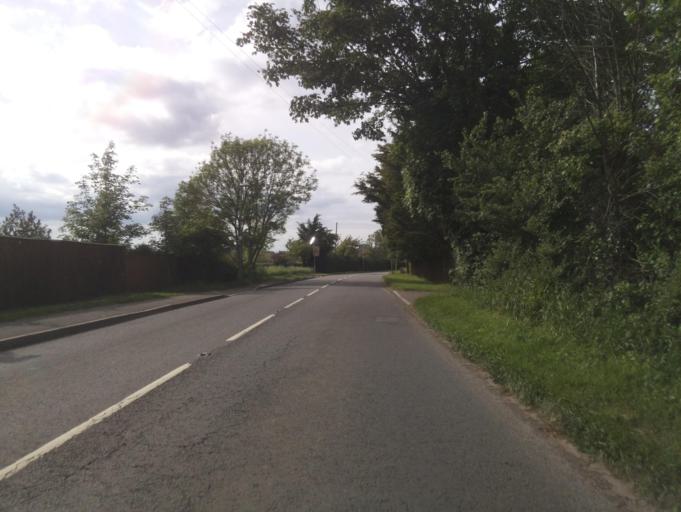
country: GB
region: England
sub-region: Worcestershire
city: South Littleton
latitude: 52.0903
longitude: -1.8610
